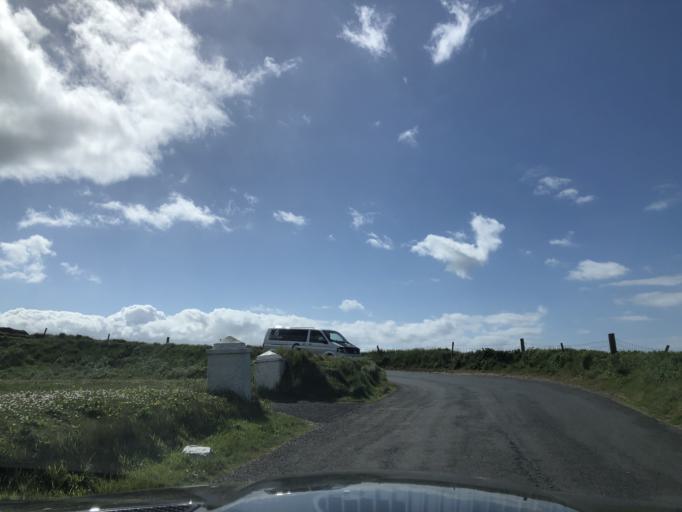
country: GB
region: Northern Ireland
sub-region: Moyle District
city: Ballycastle
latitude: 55.2441
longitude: -6.3680
